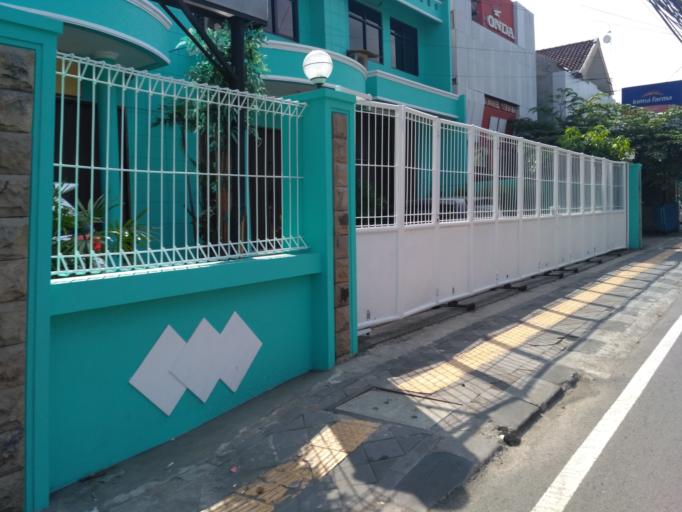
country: ID
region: Daerah Istimewa Yogyakarta
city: Depok
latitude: -7.7698
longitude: 110.4098
